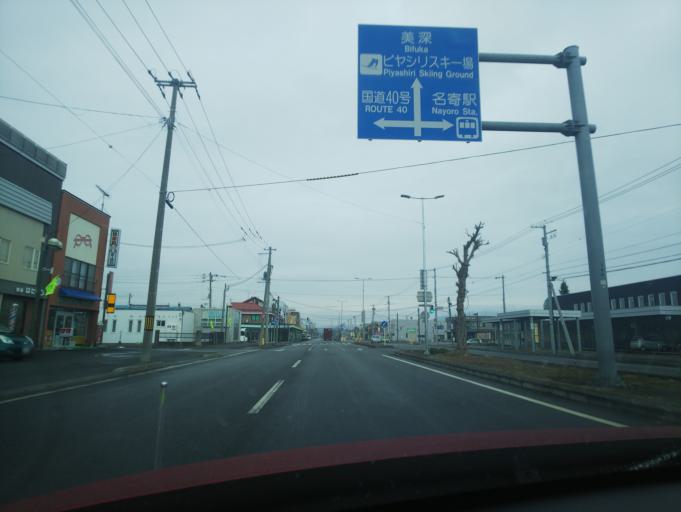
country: JP
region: Hokkaido
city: Nayoro
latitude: 44.3486
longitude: 142.4638
